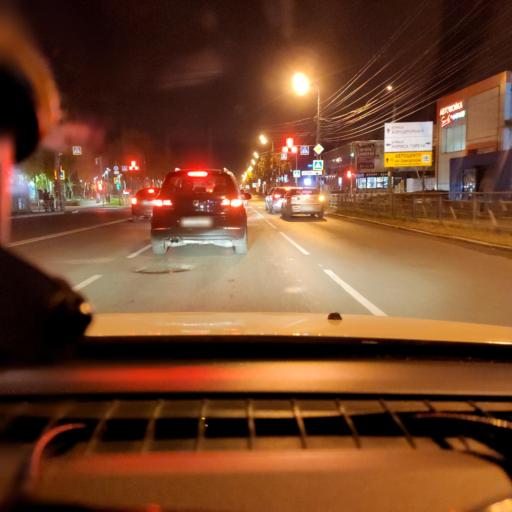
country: RU
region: Samara
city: Samara
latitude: 53.1976
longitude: 50.1903
